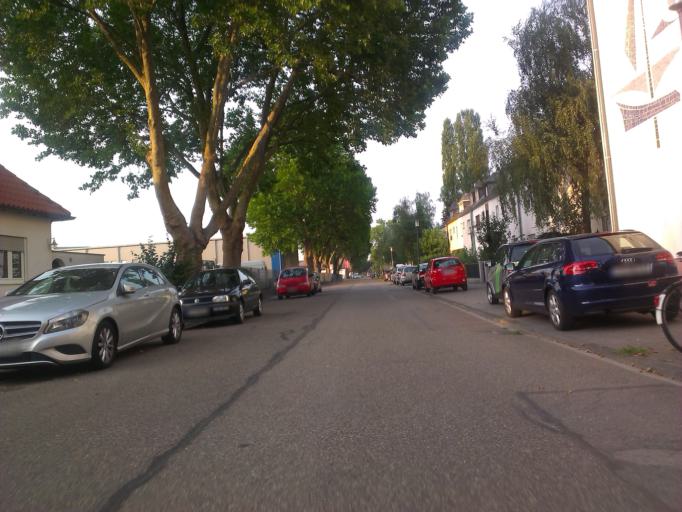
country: DE
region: Rheinland-Pfalz
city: Ludwigshafen am Rhein
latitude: 49.4654
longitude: 8.4508
